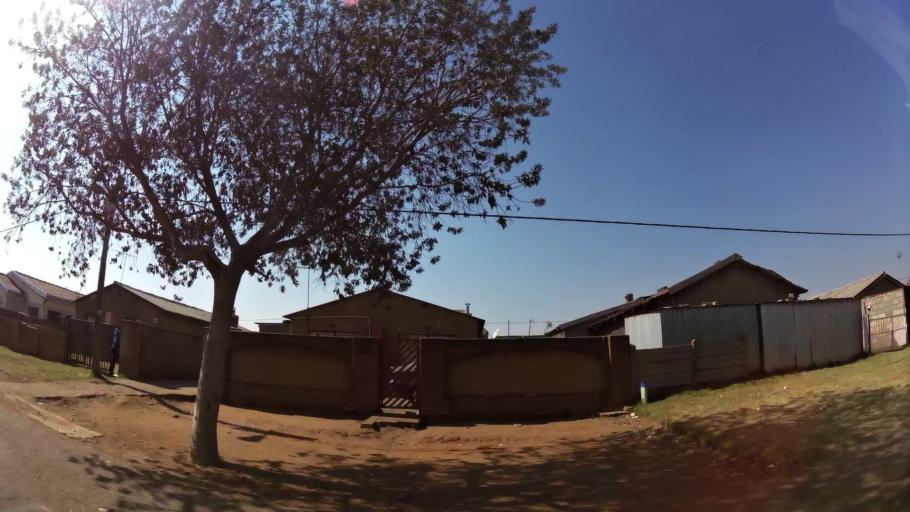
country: ZA
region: Gauteng
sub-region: Ekurhuleni Metropolitan Municipality
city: Boksburg
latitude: -26.2154
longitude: 28.2902
